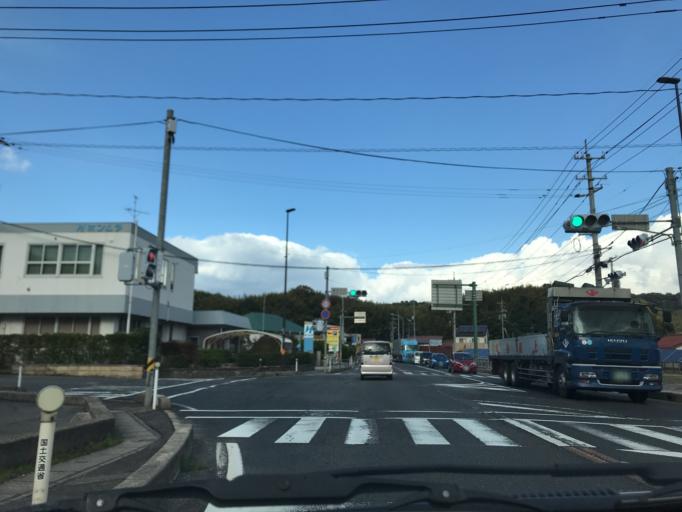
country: JP
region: Tottori
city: Yonago
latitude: 35.4155
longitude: 133.2915
